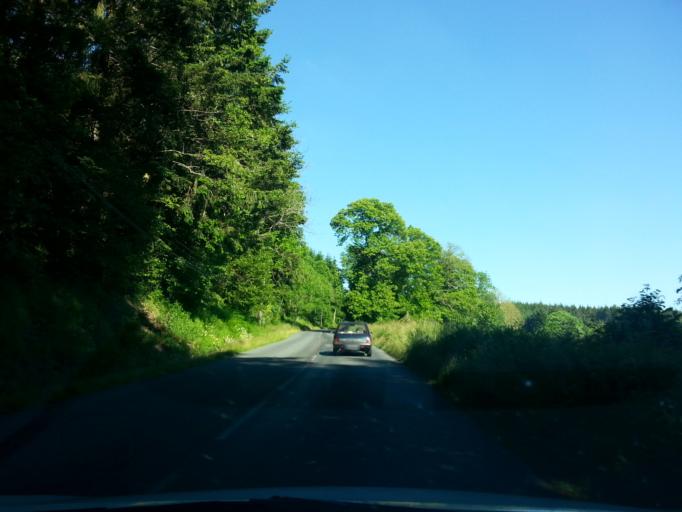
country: FR
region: Rhone-Alpes
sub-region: Departement de la Loire
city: Belmont-de-la-Loire
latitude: 46.1712
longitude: 4.4270
